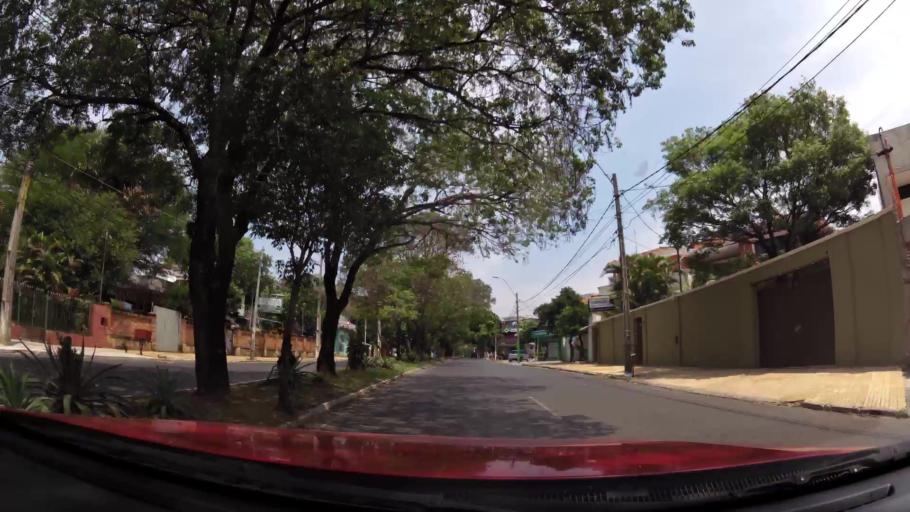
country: PY
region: Asuncion
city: Asuncion
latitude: -25.2733
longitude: -57.5987
